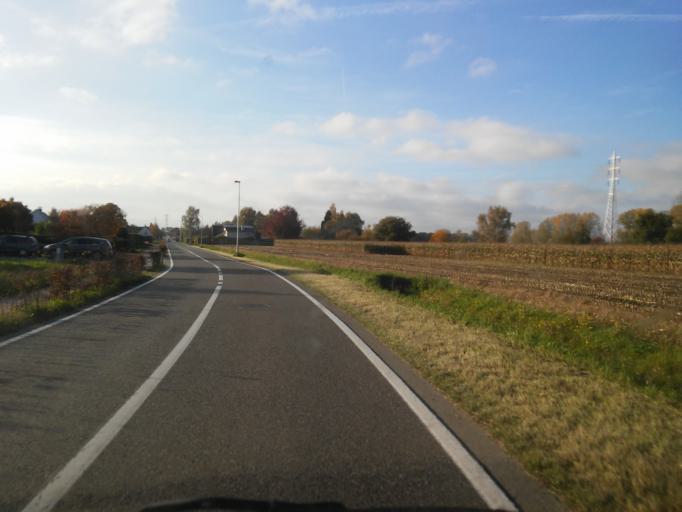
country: BE
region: Flanders
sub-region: Provincie Antwerpen
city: Duffel
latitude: 51.1003
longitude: 4.4820
